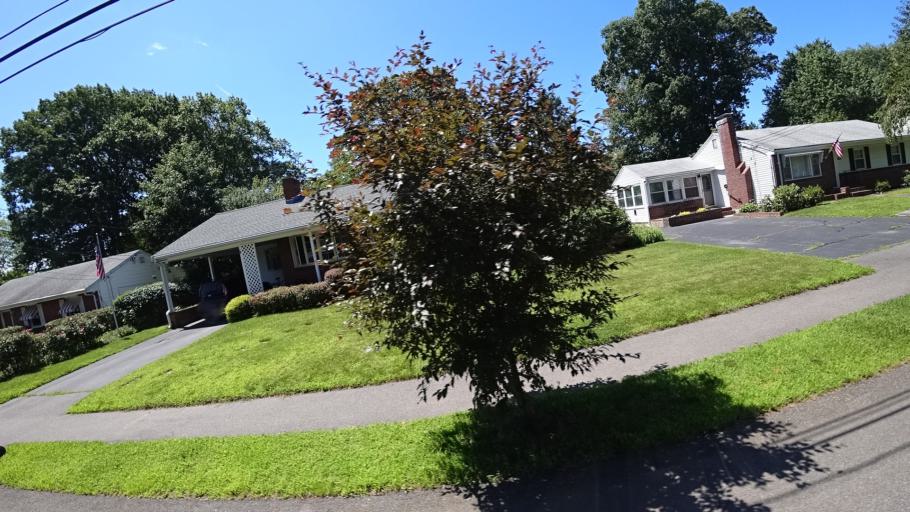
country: US
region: Massachusetts
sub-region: Norfolk County
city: Dedham
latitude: 42.2307
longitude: -71.1530
